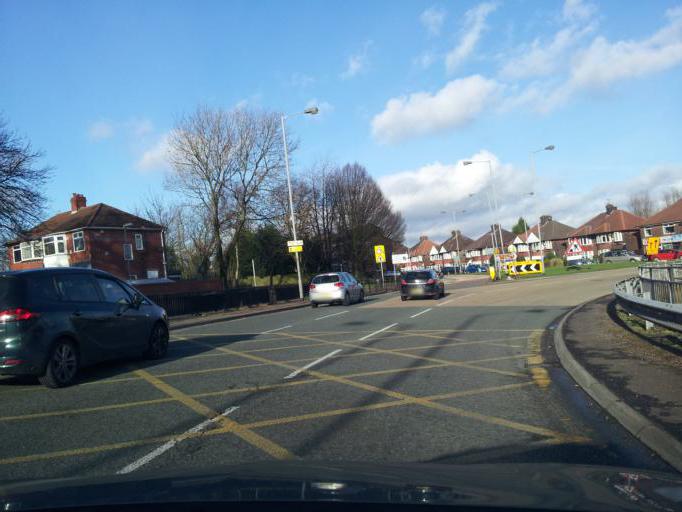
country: GB
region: England
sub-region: Borough of Bury
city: Prestwich
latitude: 53.5392
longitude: -2.2900
